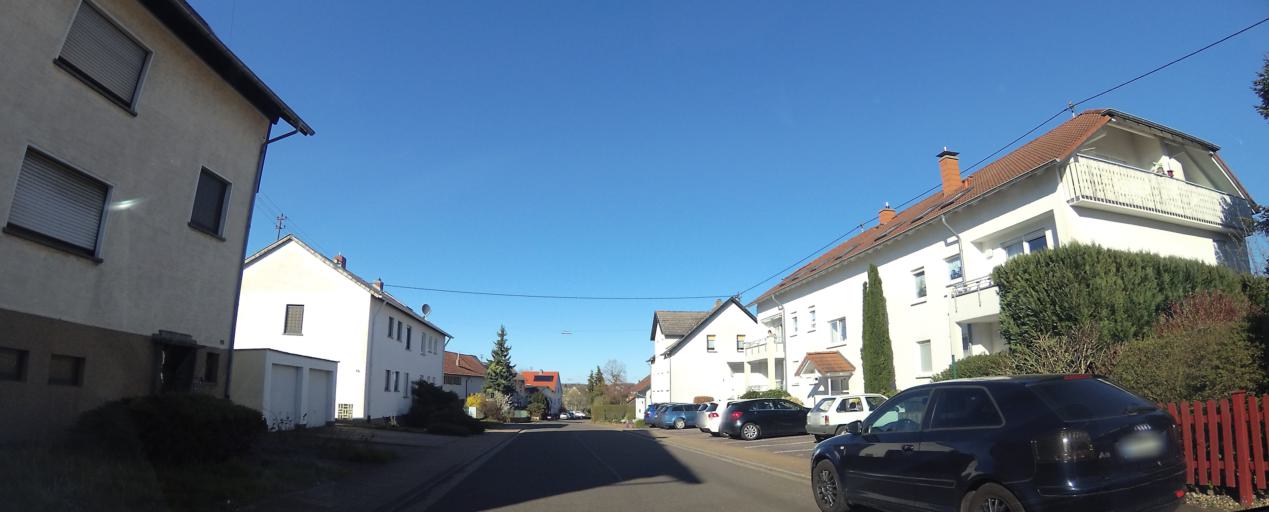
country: DE
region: Saarland
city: Riegelsberg
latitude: 49.3088
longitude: 6.9316
